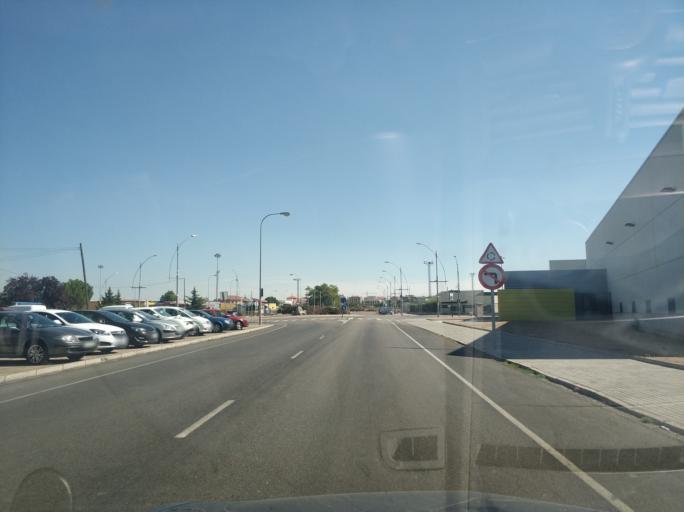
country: ES
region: Castille and Leon
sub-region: Provincia de Burgos
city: Aranda de Duero
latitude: 41.6674
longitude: -3.7029
